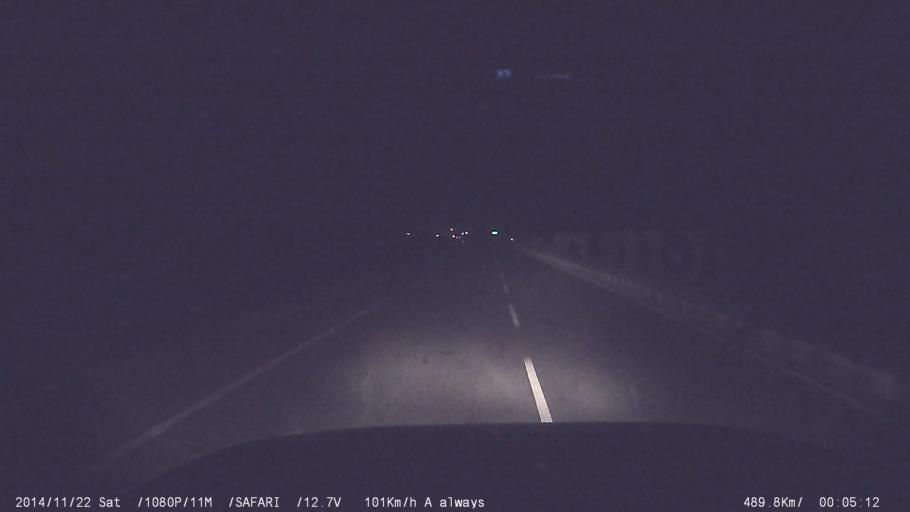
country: IN
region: Tamil Nadu
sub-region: Villupuram
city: Kallakkurichchi
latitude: 11.7305
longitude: 79.1009
